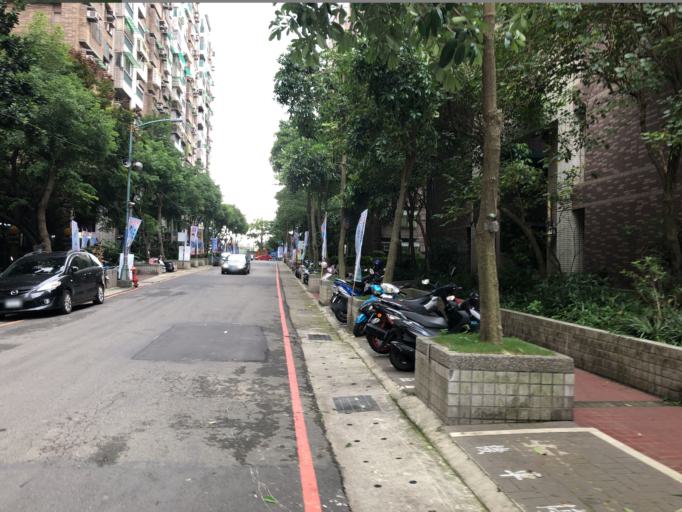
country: TW
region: Taiwan
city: Taoyuan City
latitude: 24.9666
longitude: 121.2518
